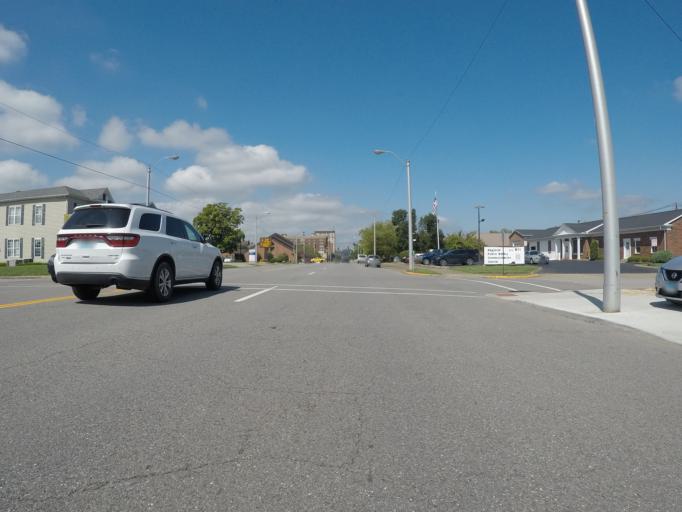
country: US
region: Kentucky
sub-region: Boyd County
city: Ashland
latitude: 38.4758
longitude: -82.6337
